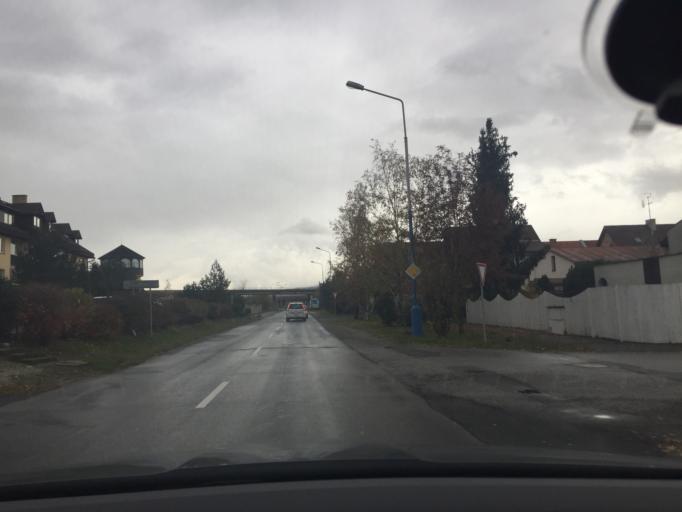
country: SK
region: Presovsky
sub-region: Okres Poprad
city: Poprad
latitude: 49.0655
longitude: 20.2722
